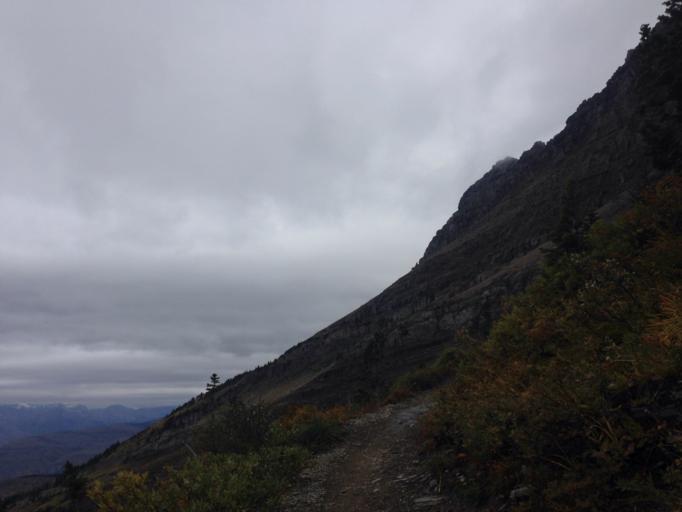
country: US
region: Montana
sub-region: Flathead County
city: Columbia Falls
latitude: 48.7410
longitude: -113.7291
